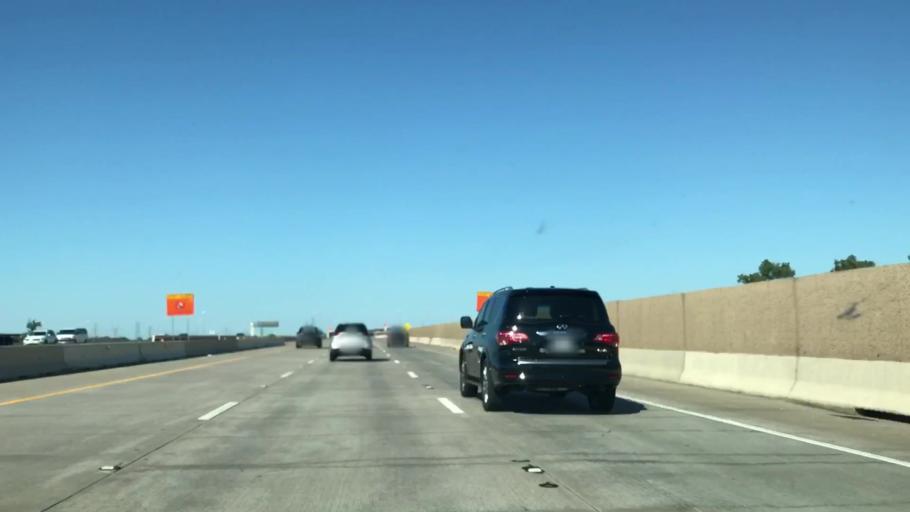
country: US
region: Texas
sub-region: Dallas County
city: Carrollton
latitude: 32.9676
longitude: -96.9326
